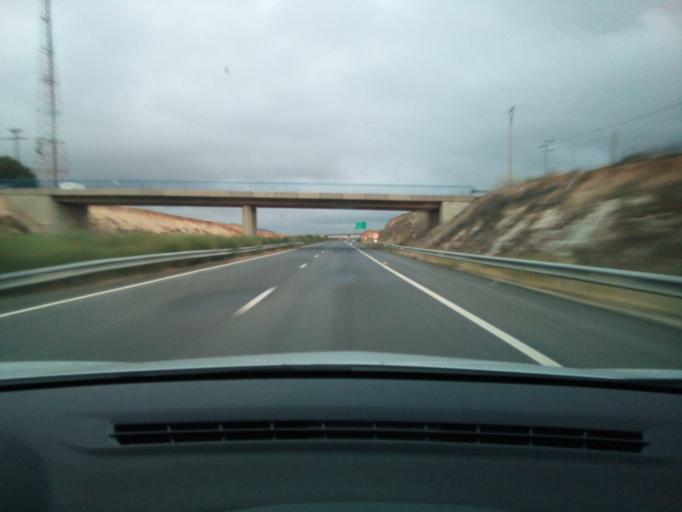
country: MA
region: Meknes-Tafilalet
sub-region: Meknes
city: Meknes
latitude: 33.8456
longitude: -5.6103
